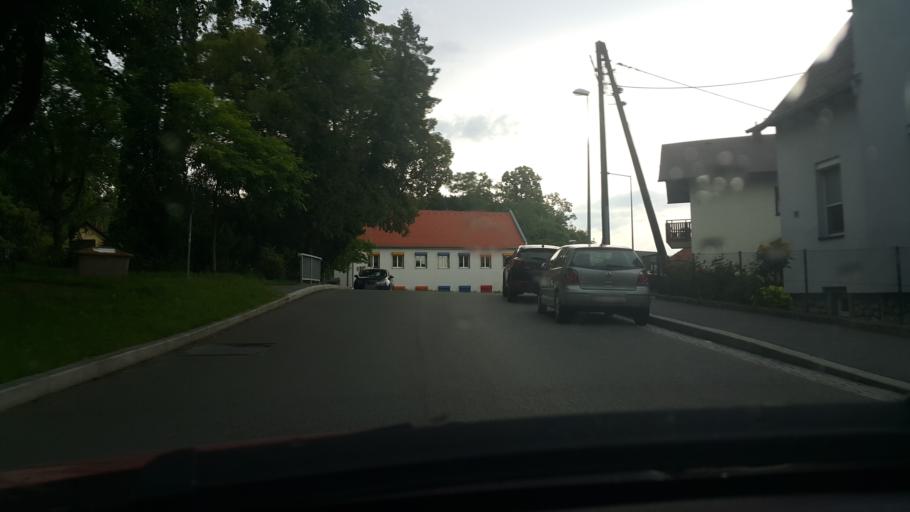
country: AT
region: Styria
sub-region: Graz Stadt
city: Wetzelsdorf
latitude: 47.0580
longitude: 15.3890
